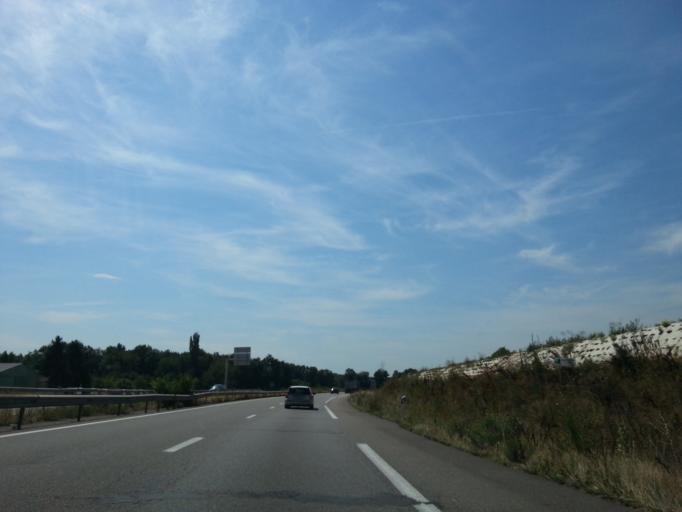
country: FR
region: Alsace
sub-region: Departement du Haut-Rhin
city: Ostheim
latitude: 48.1591
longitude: 7.3790
